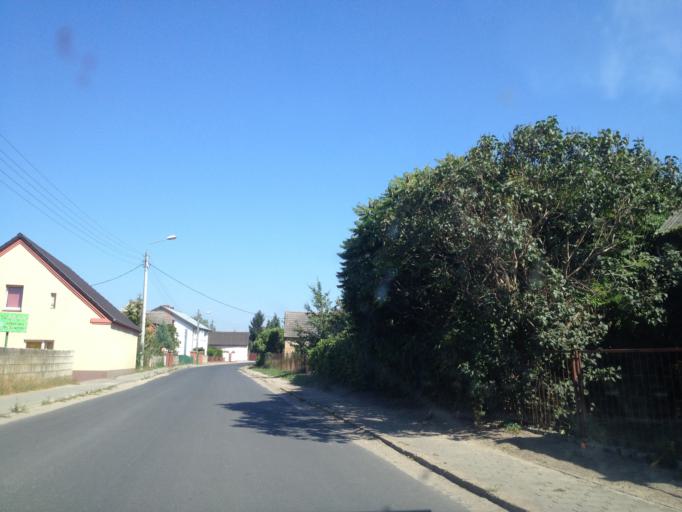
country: PL
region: Greater Poland Voivodeship
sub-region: Powiat sredzki
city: Zaniemysl
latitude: 52.1141
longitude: 17.1167
